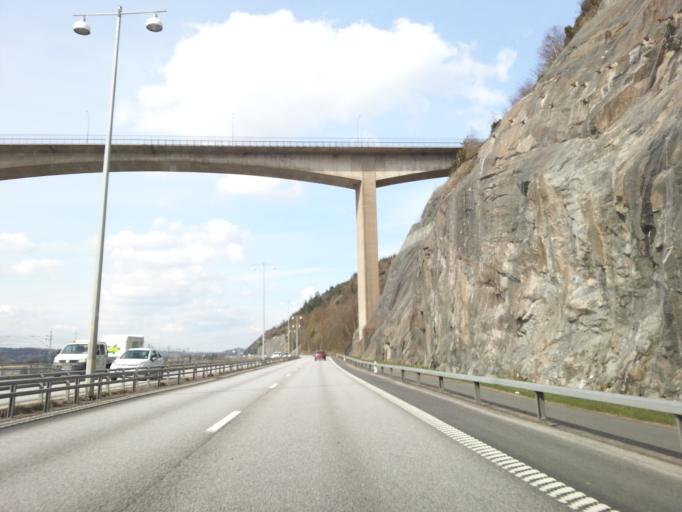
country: SE
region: Vaestra Goetaland
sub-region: Goteborg
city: Gardsten
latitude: 57.7982
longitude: 12.0161
